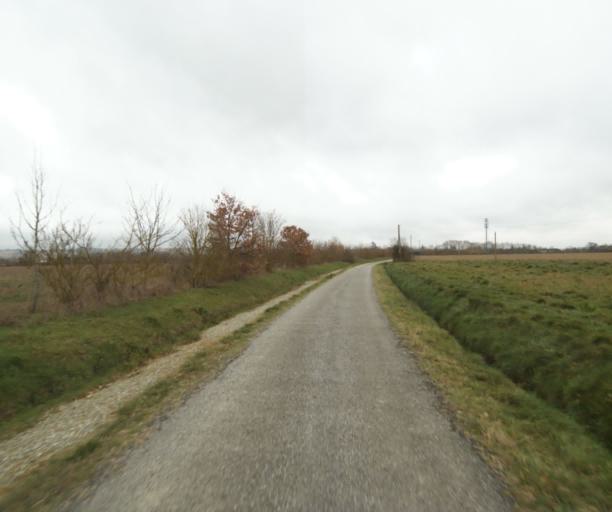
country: FR
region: Midi-Pyrenees
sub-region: Departement de l'Ariege
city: Mazeres
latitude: 43.2508
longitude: 1.6611
